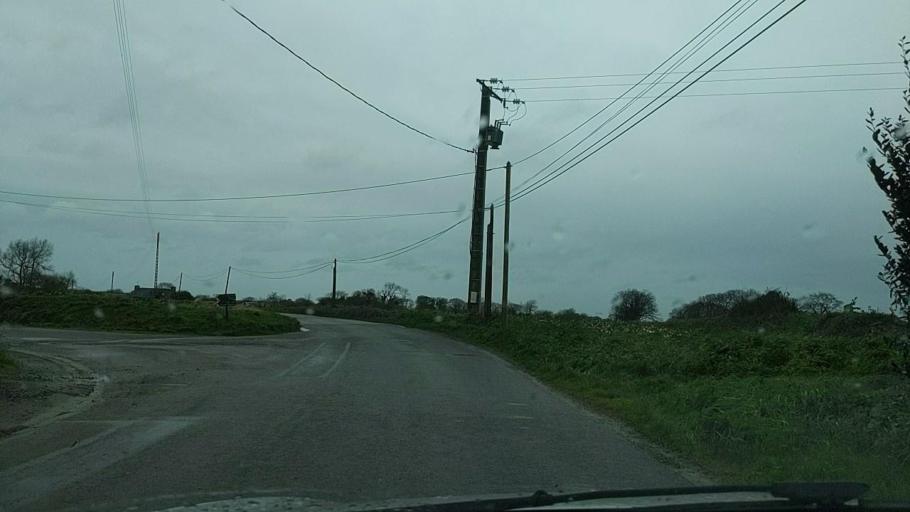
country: FR
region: Brittany
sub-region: Departement des Cotes-d'Armor
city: Pleumeur-Gautier
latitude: 48.8048
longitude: -3.1612
